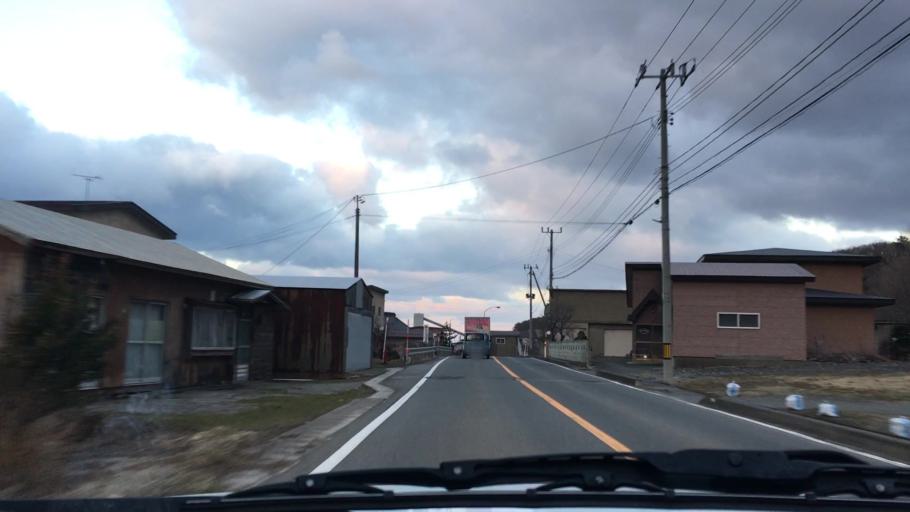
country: JP
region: Aomori
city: Shimokizukuri
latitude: 40.7484
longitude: 140.1411
